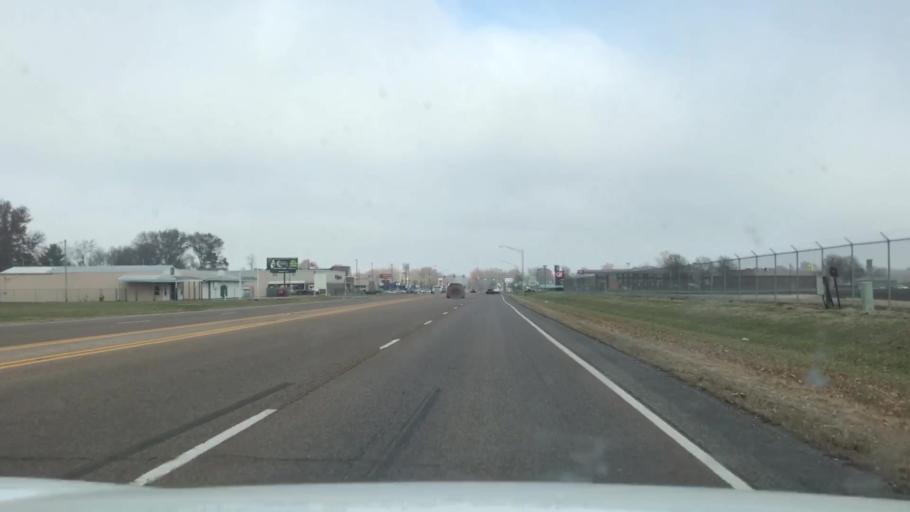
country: US
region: Illinois
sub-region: Madison County
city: Bethalto
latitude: 38.8980
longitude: -90.0593
